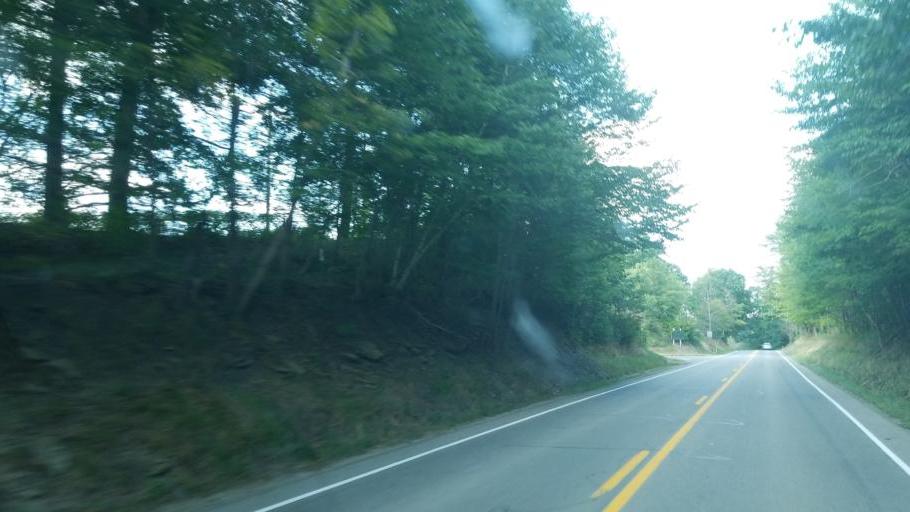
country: US
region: Pennsylvania
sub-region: Clarion County
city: Knox
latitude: 41.2219
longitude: -79.5319
